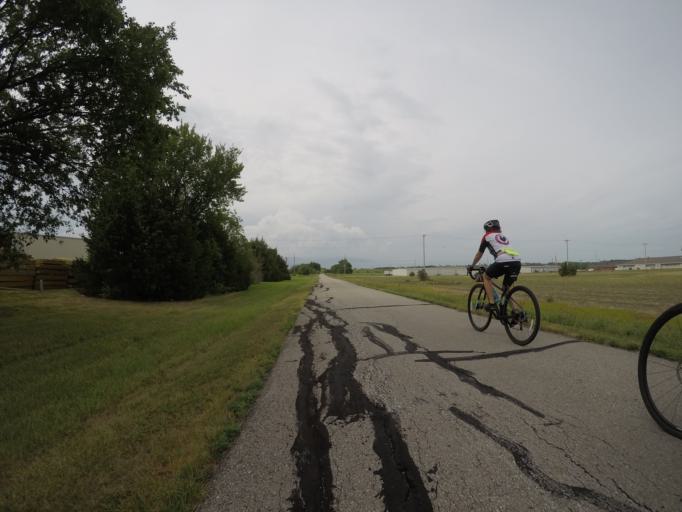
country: US
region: Kansas
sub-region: Franklin County
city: Ottawa
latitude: 38.5815
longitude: -95.2709
